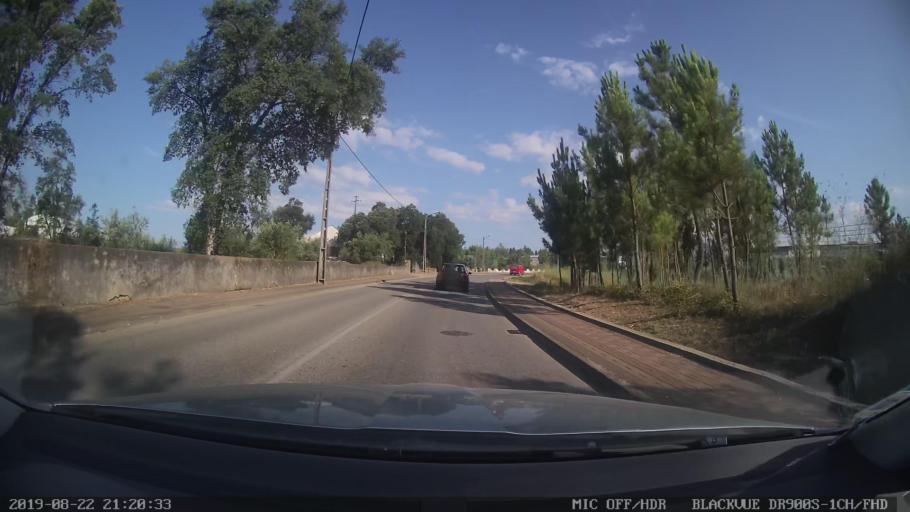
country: PT
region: Castelo Branco
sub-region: Serta
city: Serta
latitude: 39.8133
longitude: -8.1086
